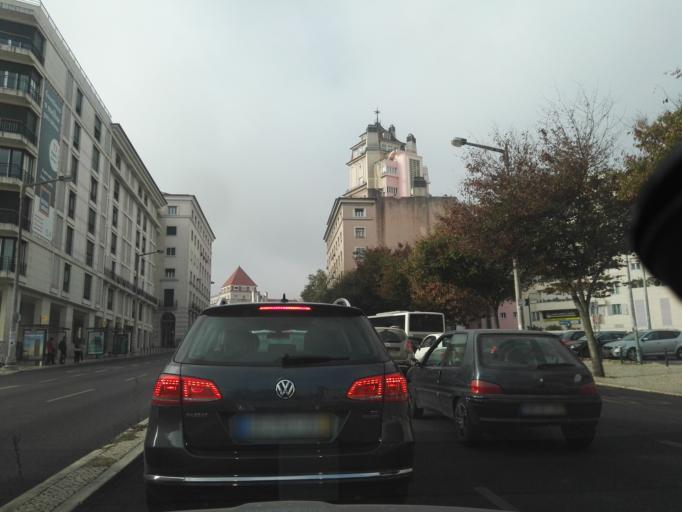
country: PT
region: Lisbon
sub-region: Lisbon
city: Lisbon
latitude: 38.7438
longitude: -9.1323
